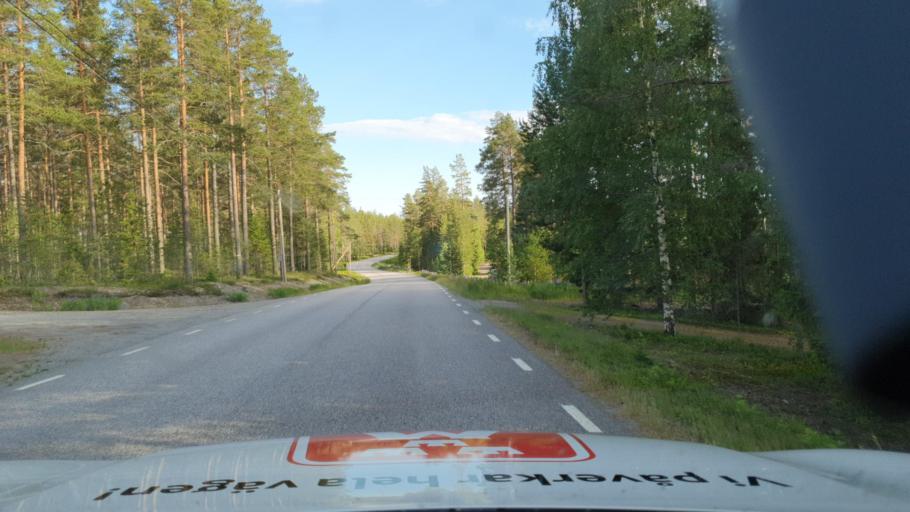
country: SE
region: Vaesterbotten
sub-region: Umea Kommun
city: Roback
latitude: 63.9031
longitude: 20.1534
